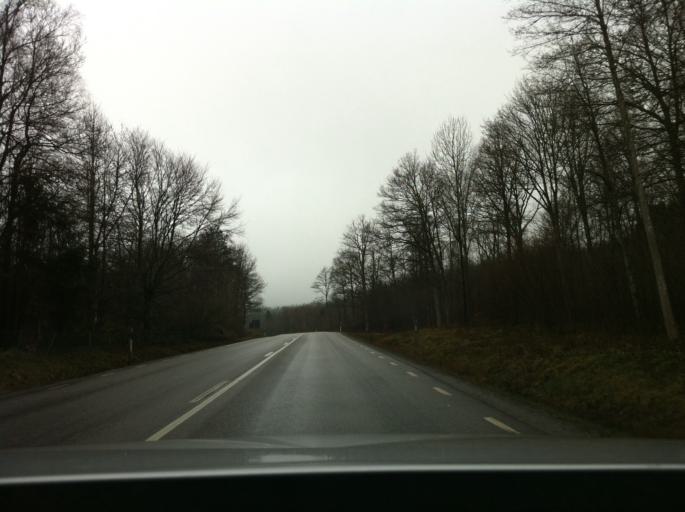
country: SE
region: Vaestra Goetaland
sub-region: Alingsas Kommun
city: Sollebrunn
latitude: 58.0623
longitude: 12.4705
